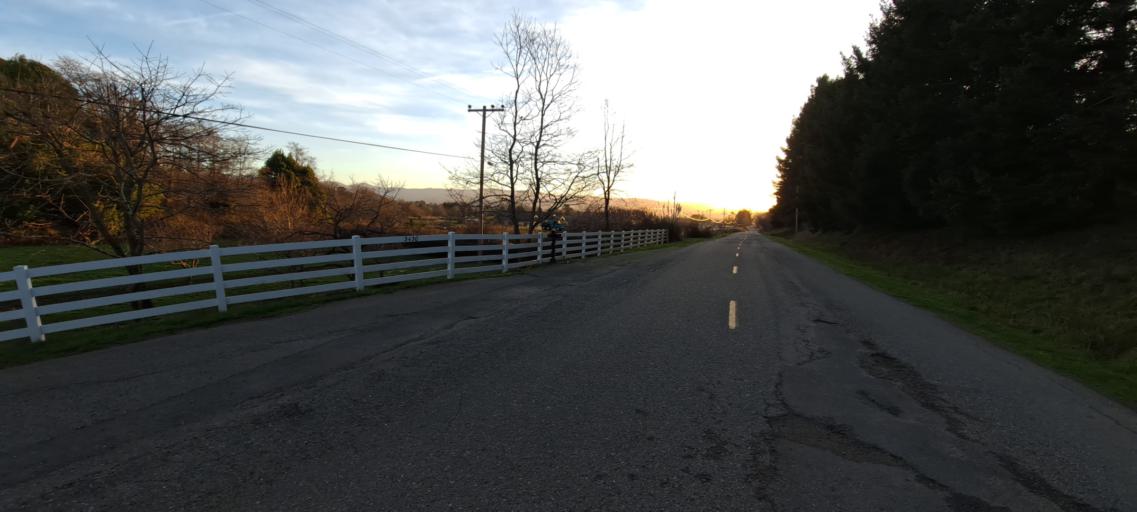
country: US
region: California
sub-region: Humboldt County
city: Fortuna
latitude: 40.5964
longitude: -124.1308
